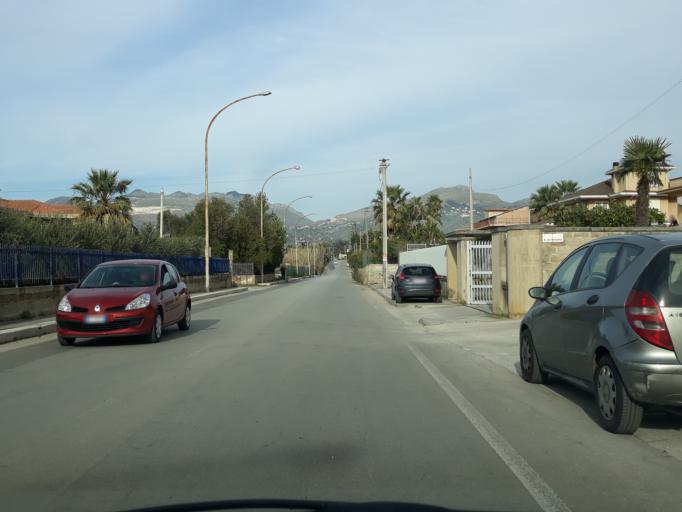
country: IT
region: Sicily
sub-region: Palermo
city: Borgetto
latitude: 38.0579
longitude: 13.1336
